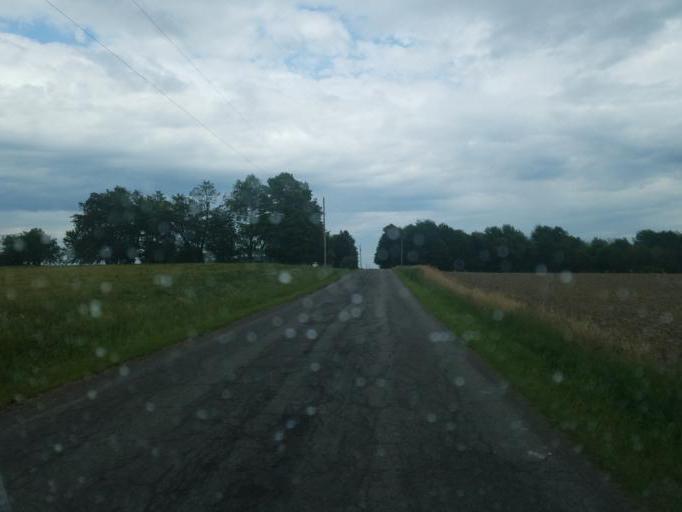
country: US
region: Ohio
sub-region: Richland County
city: Lexington
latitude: 40.6013
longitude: -82.6857
